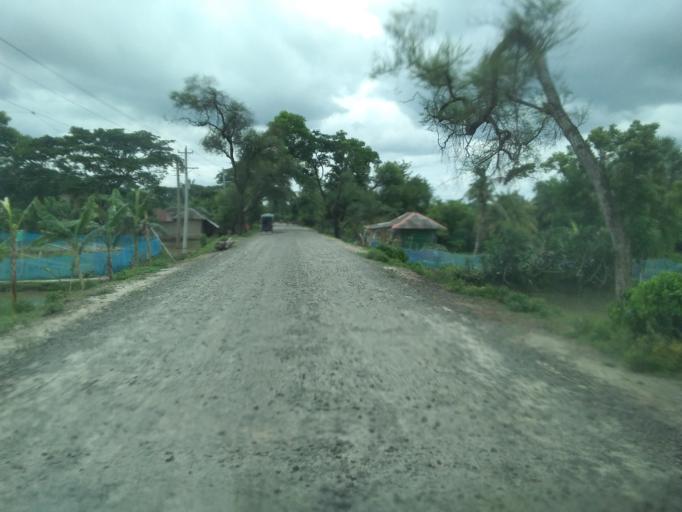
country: IN
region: West Bengal
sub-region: North 24 Parganas
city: Gosaba
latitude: 22.2670
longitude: 89.1654
